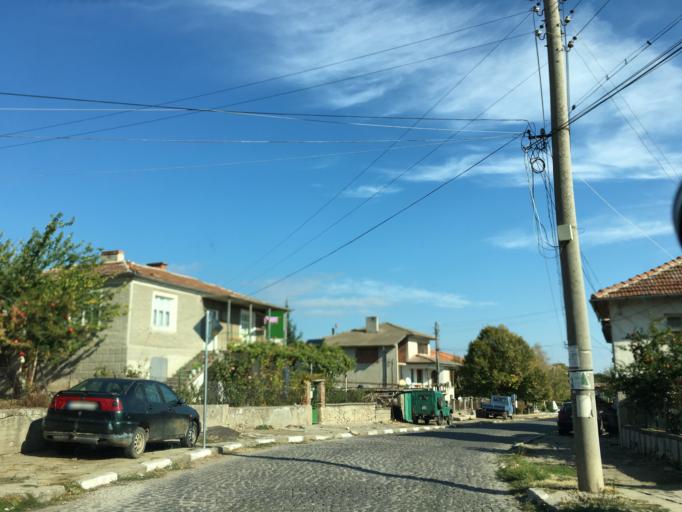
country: BG
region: Khaskovo
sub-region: Obshtina Ivaylovgrad
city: Ivaylovgrad
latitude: 41.5129
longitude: 26.1124
